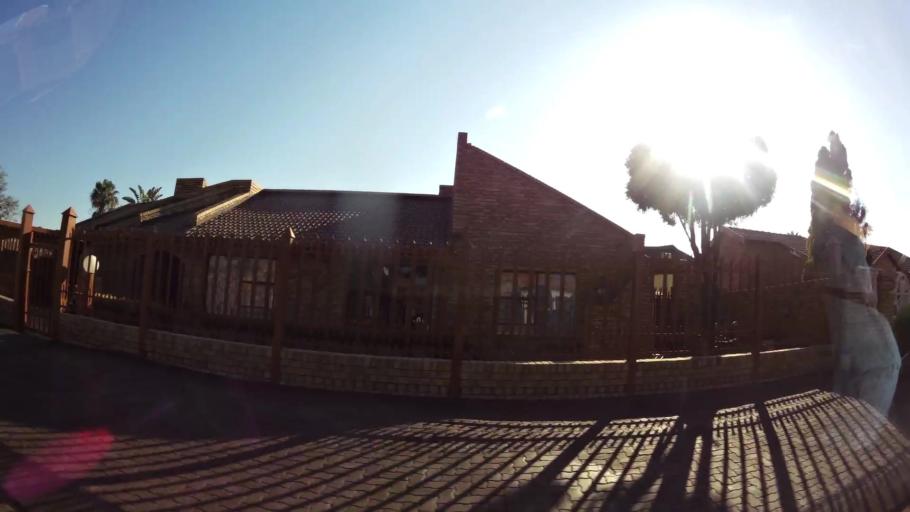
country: ZA
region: Gauteng
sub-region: City of Tshwane Metropolitan Municipality
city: Pretoria
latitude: -25.6700
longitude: 28.2190
